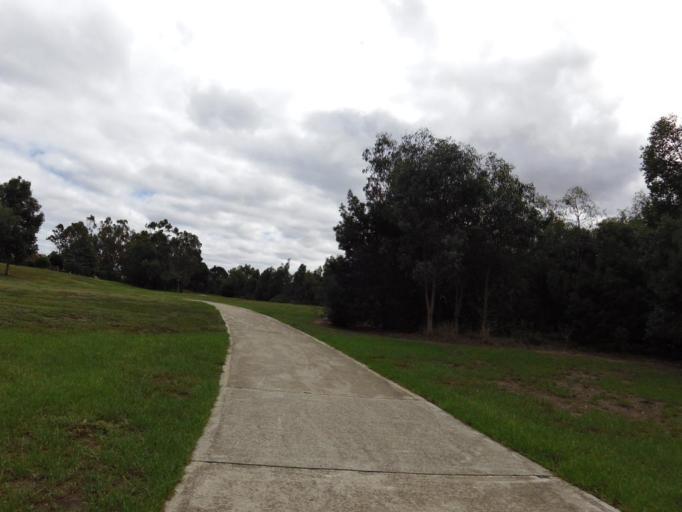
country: AU
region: Victoria
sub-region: Wyndham
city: Werribee
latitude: -37.8928
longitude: 144.6509
